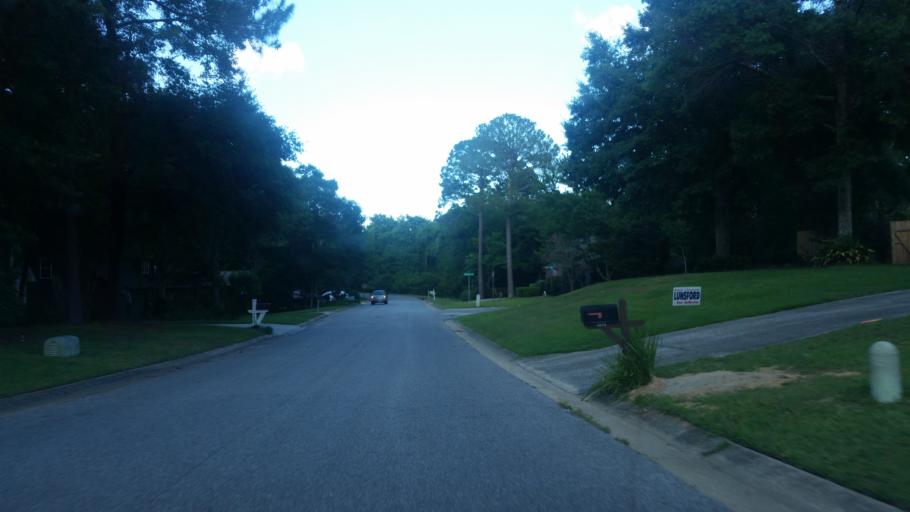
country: US
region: Florida
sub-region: Escambia County
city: Ferry Pass
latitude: 30.5112
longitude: -87.1673
